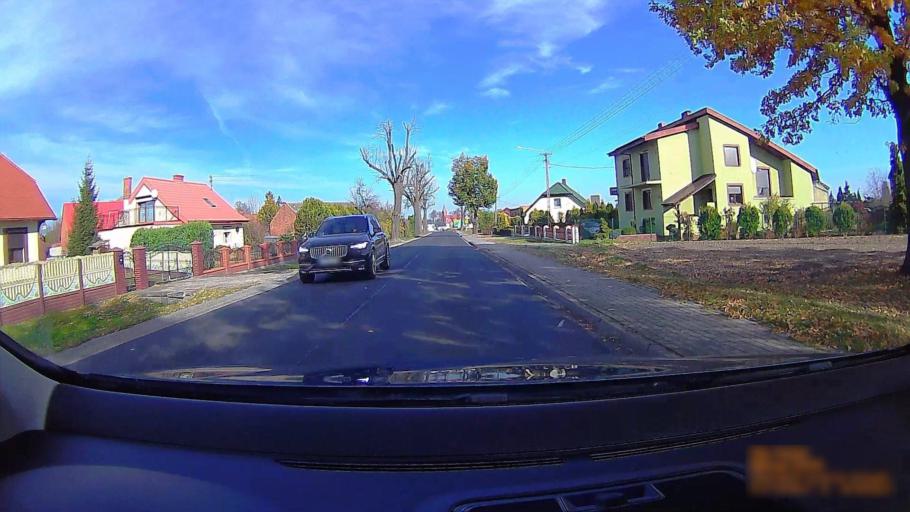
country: PL
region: Greater Poland Voivodeship
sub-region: Powiat ostrzeszowski
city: Doruchow
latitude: 51.4107
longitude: 18.0750
